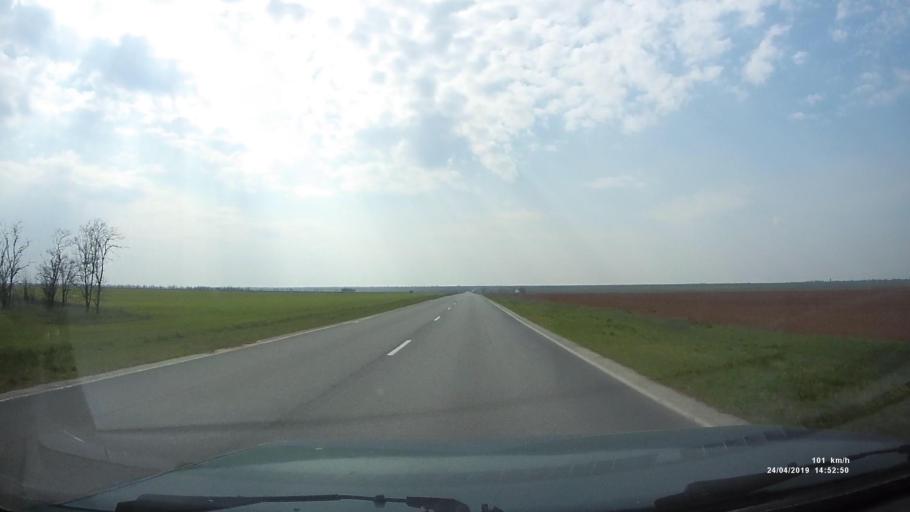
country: RU
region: Rostov
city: Remontnoye
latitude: 46.5307
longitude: 43.6720
